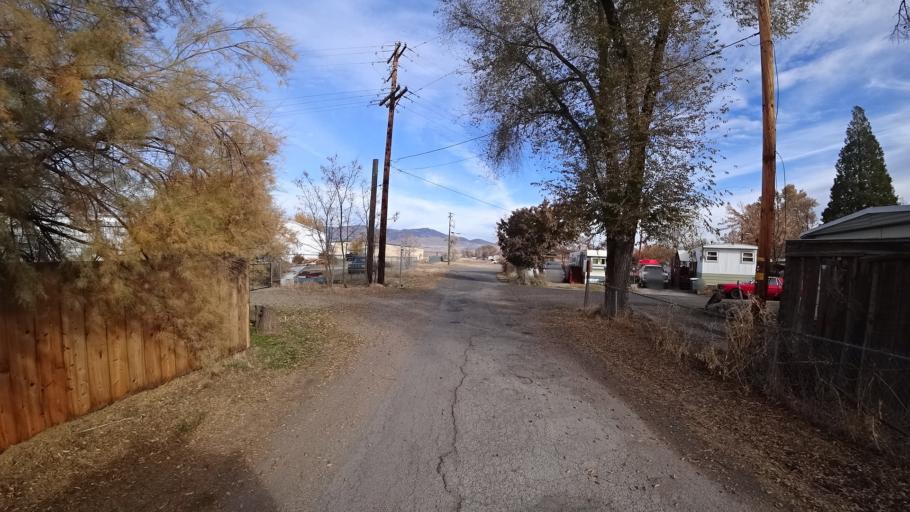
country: US
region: California
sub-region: Siskiyou County
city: Montague
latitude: 41.7276
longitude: -122.5348
